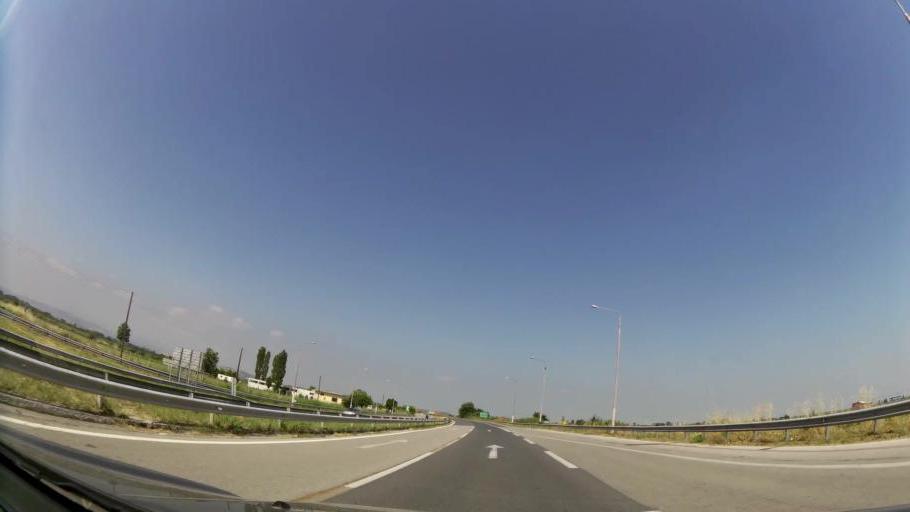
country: GR
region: Central Macedonia
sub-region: Nomos Imathias
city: Kleidi
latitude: 40.5595
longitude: 22.5859
